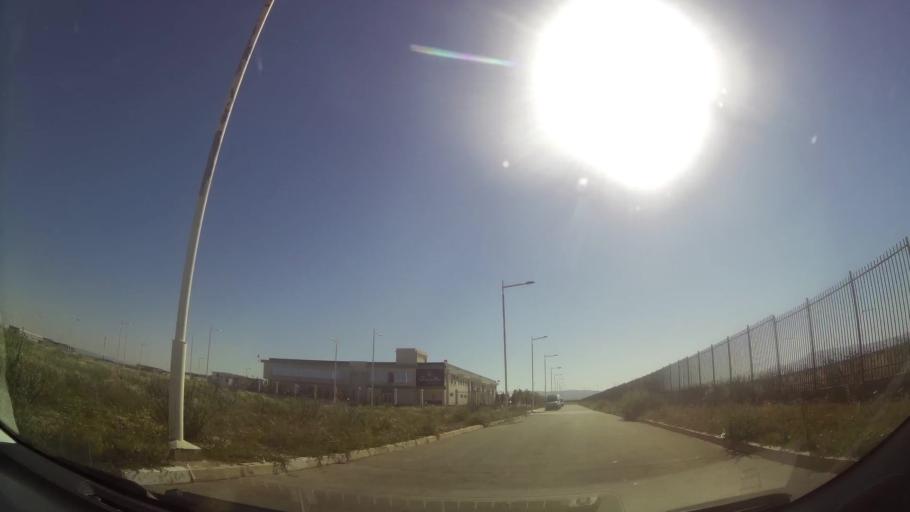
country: MA
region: Oriental
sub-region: Oujda-Angad
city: Oujda
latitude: 34.7760
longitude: -1.9332
